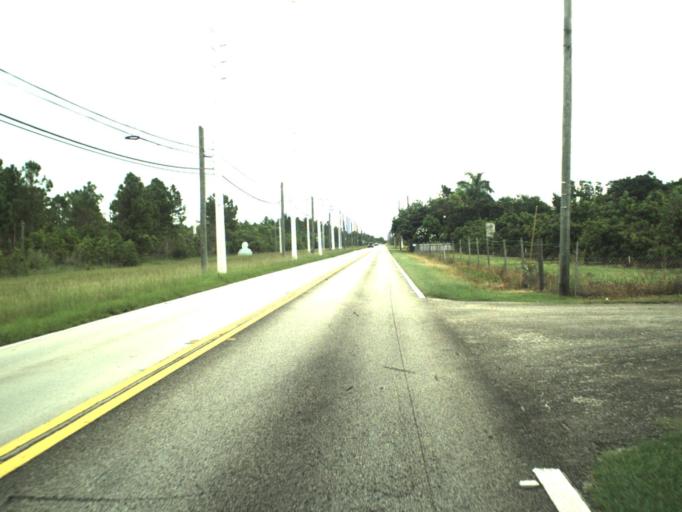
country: US
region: Florida
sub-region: Miami-Dade County
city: Florida City
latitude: 25.4366
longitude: -80.5015
